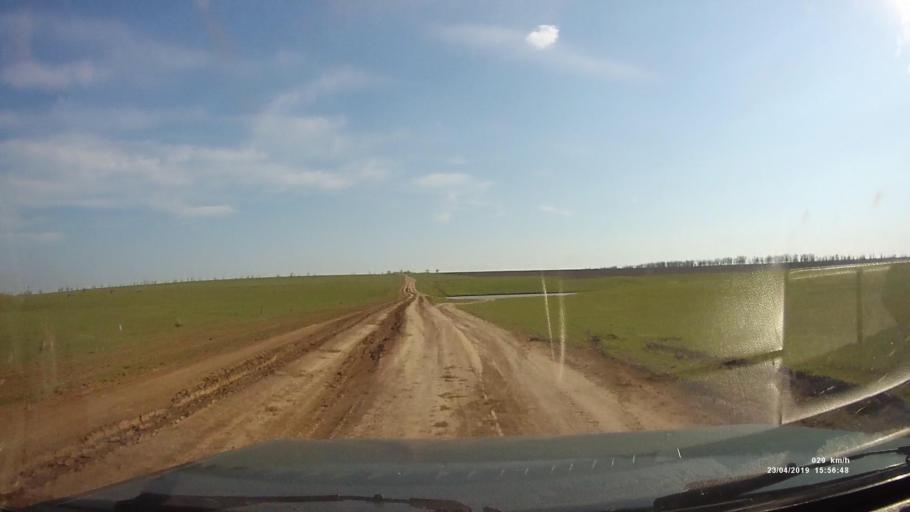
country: RU
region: Rostov
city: Remontnoye
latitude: 46.5353
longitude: 43.1107
